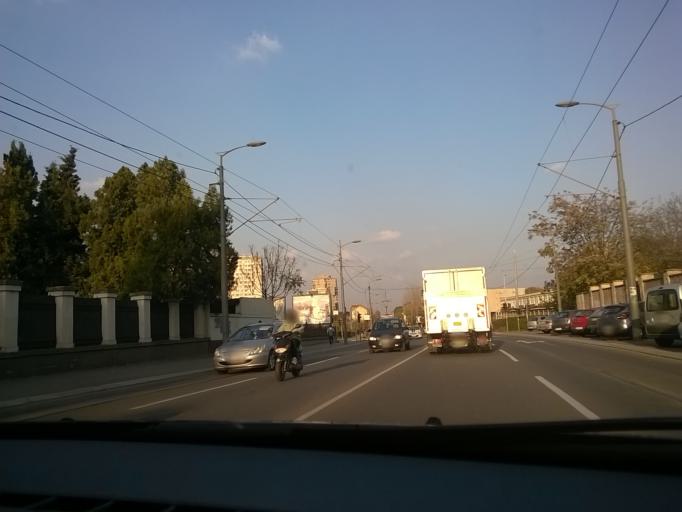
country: RS
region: Central Serbia
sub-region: Belgrade
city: Vracar
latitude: 44.8109
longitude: 20.4866
